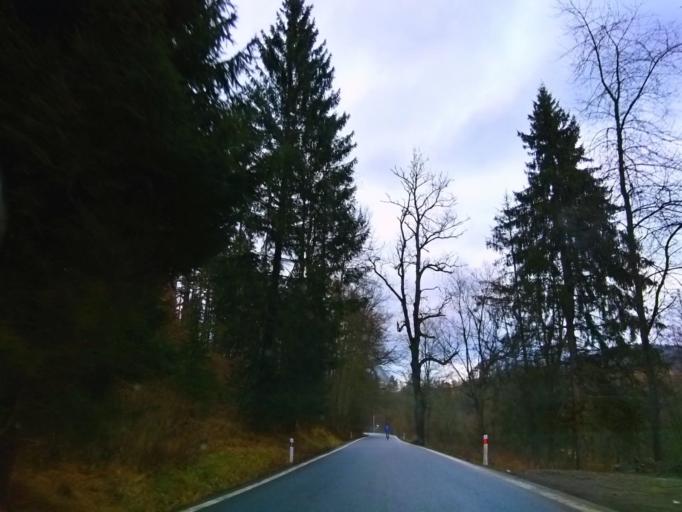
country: CZ
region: Jihocesky
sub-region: Okres Cesky Krumlov
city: Vyssi Brod
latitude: 48.6606
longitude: 14.3643
